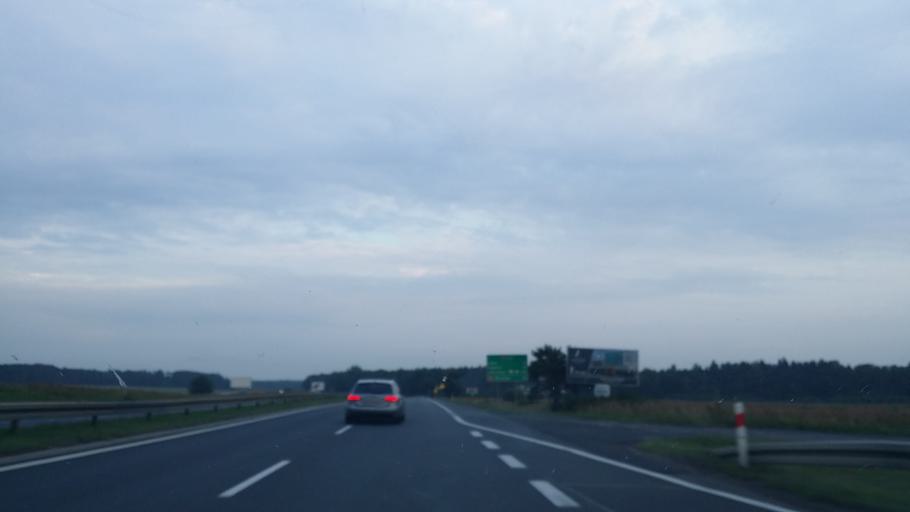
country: PL
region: Lower Silesian Voivodeship
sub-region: Powiat polkowicki
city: Polkowice
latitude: 51.4895
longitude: 16.0786
